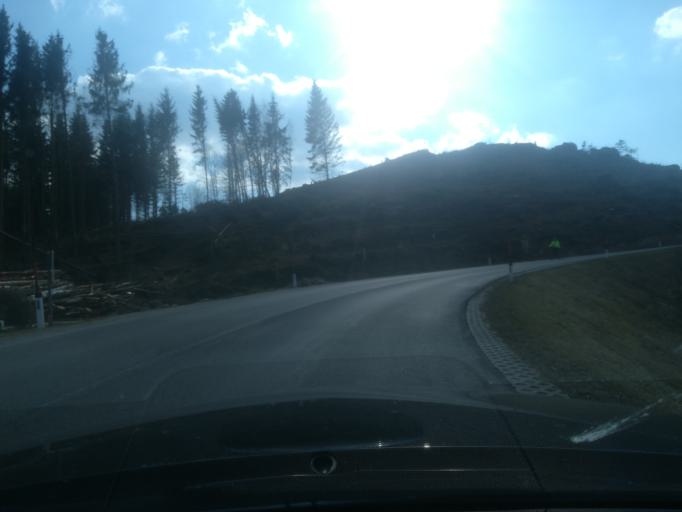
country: AT
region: Upper Austria
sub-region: Politischer Bezirk Freistadt
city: Freistadt
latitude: 48.4457
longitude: 14.6887
